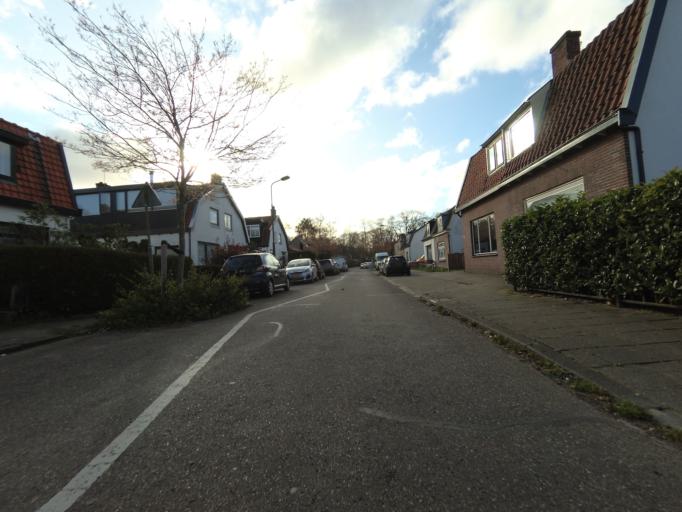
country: NL
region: Utrecht
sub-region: Gemeente Utrechtse Heuvelrug
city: Driebergen-Rijsenburg
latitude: 52.0546
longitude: 5.2939
